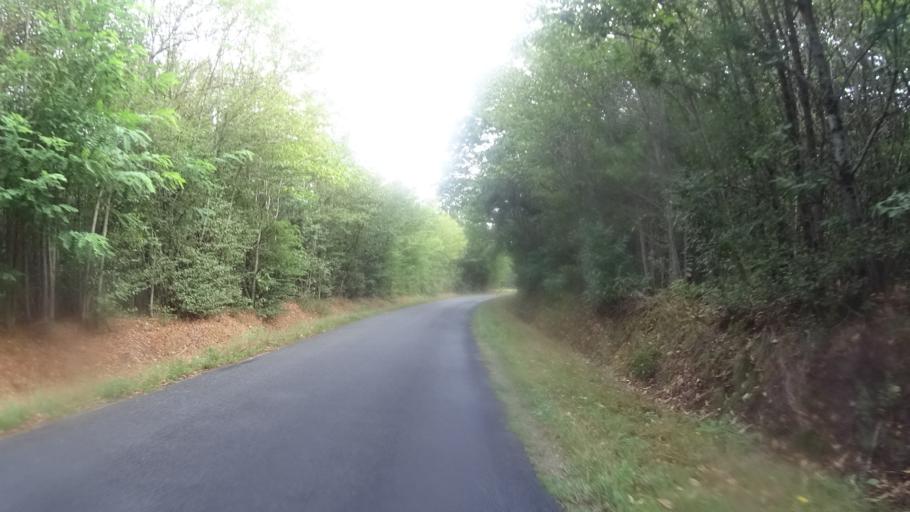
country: FR
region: Centre
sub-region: Departement du Loiret
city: Fay-aux-Loges
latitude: 47.9679
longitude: 2.1845
